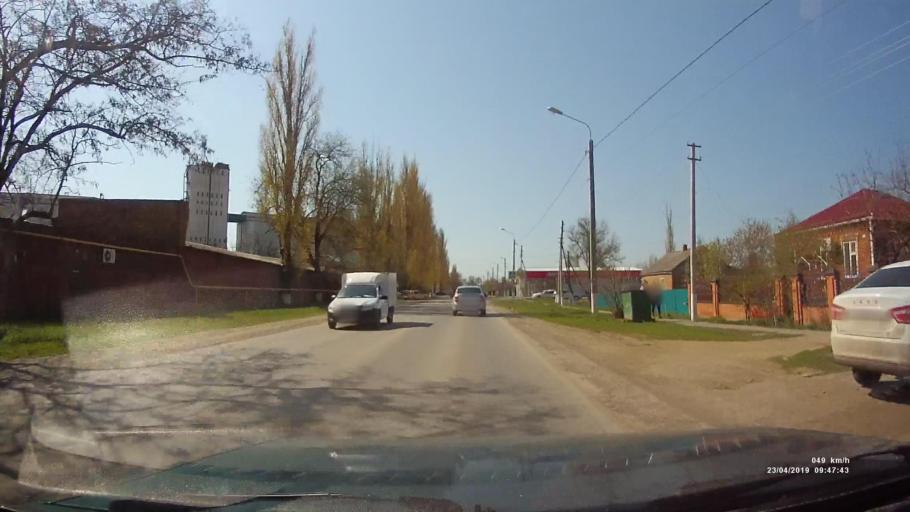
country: RU
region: Rostov
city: Orlovskiy
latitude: 46.8733
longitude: 42.0384
